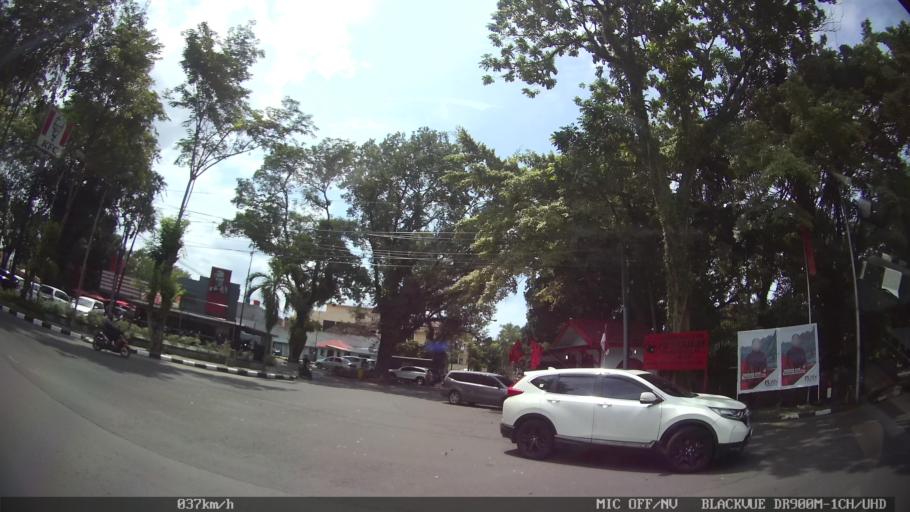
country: ID
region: North Sumatra
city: Medan
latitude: 3.5714
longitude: 98.6714
